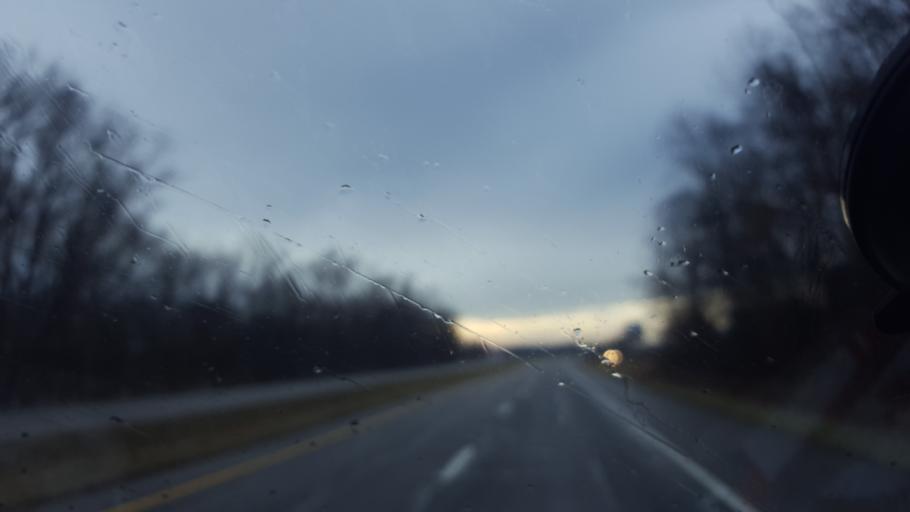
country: US
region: Ohio
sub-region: Coshocton County
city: West Lafayette
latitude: 40.2851
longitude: -81.6985
